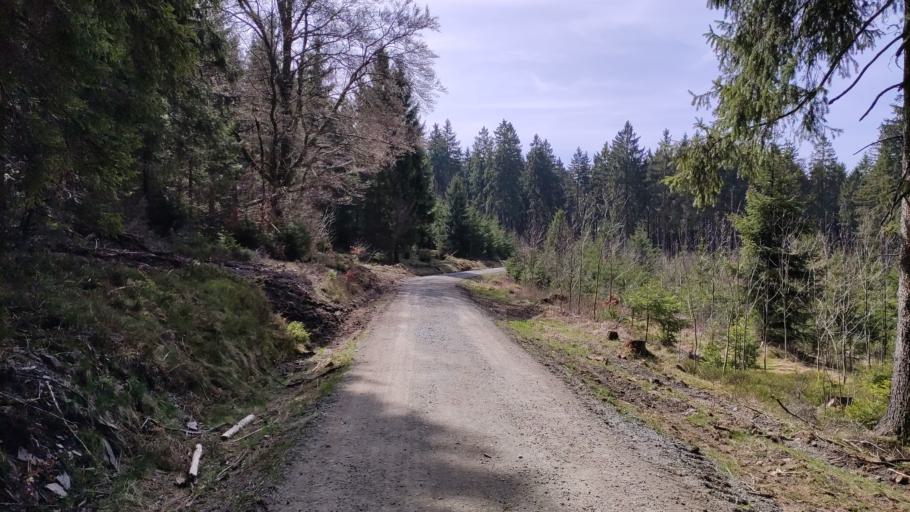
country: DE
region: Bavaria
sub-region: Upper Franconia
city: Reichenbach
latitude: 50.4458
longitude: 11.4443
